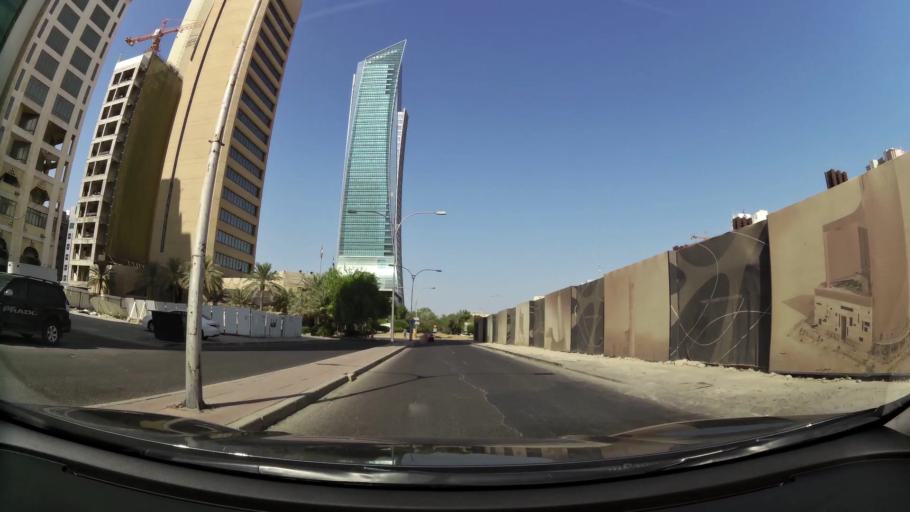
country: KW
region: Al Asimah
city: Kuwait City
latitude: 29.3842
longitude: 47.9888
